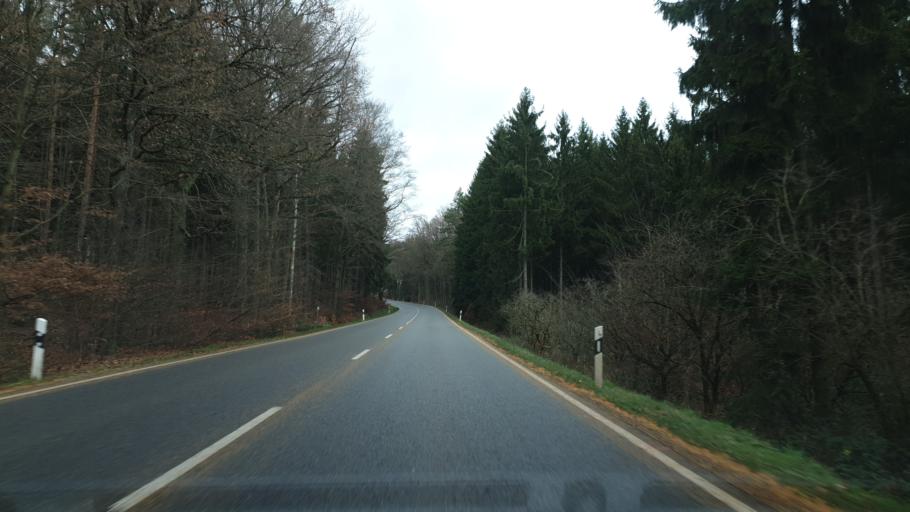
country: DE
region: Saxony
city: Bernsdorf
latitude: 50.8004
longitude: 12.6718
